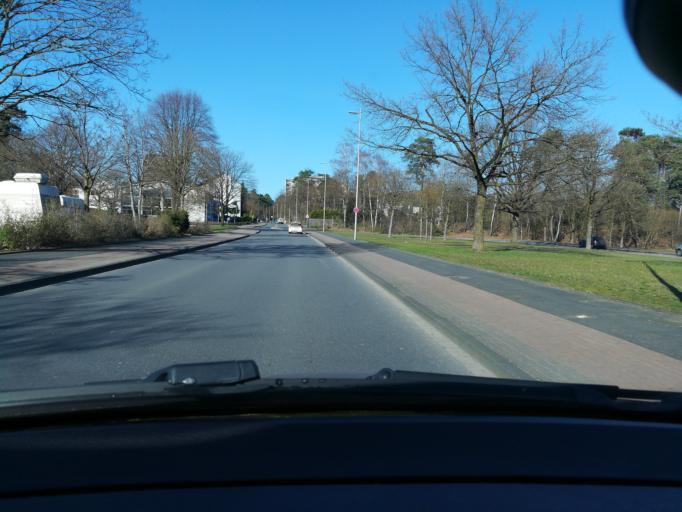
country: DE
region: North Rhine-Westphalia
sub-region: Regierungsbezirk Detmold
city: Oerlinghausen
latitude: 51.9531
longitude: 8.5967
